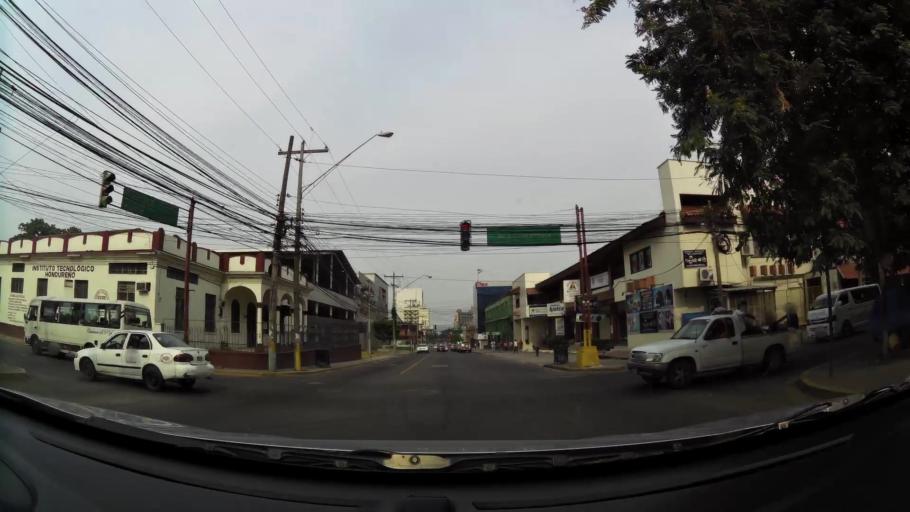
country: HN
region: Cortes
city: San Pedro Sula
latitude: 15.5061
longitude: -88.0285
